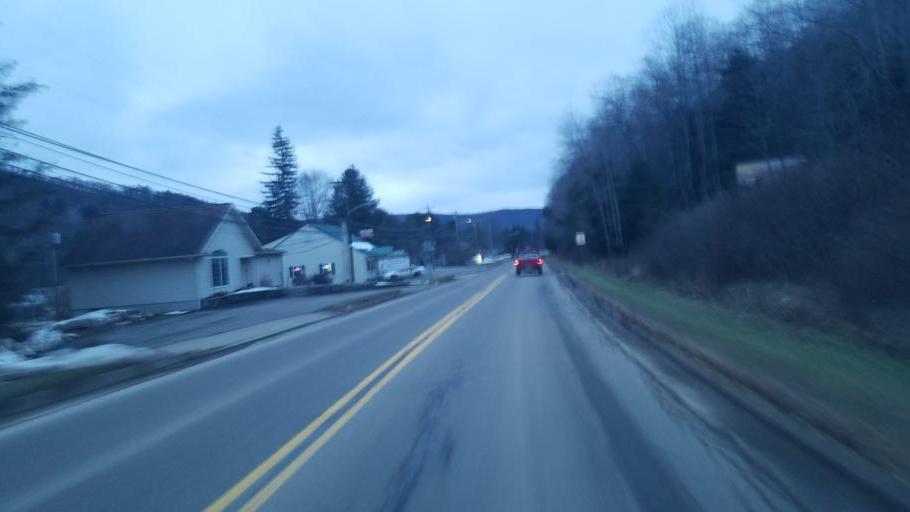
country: US
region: Pennsylvania
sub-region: Potter County
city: Coudersport
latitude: 41.7853
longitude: -78.0172
